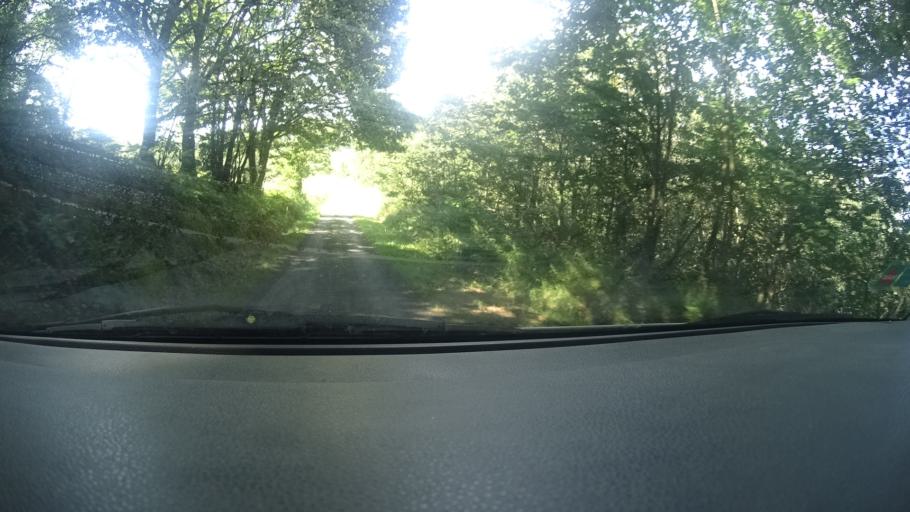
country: FR
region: Aquitaine
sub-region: Departement des Pyrenees-Atlantiques
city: Mont
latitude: 43.4990
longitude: -0.6899
